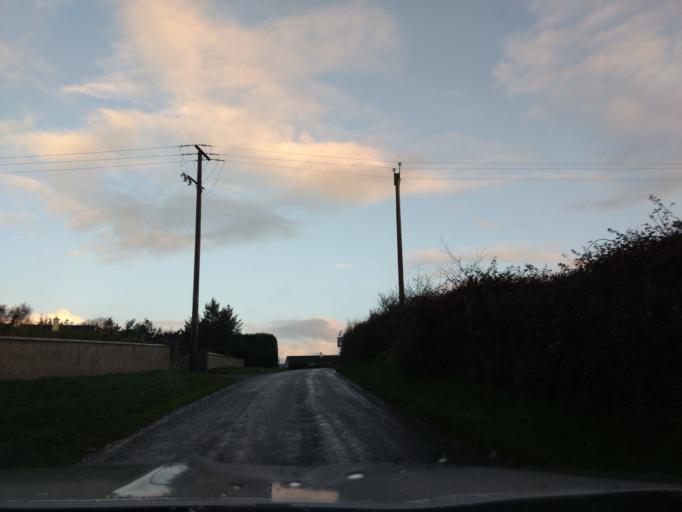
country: IE
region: Ulster
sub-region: County Donegal
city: Buncrana
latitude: 55.0962
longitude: -7.5421
